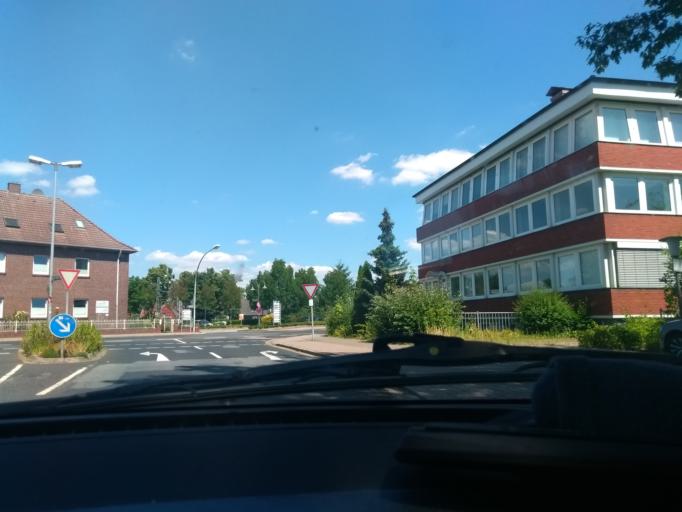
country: DE
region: Lower Saxony
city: Meppen
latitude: 52.6936
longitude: 7.3001
